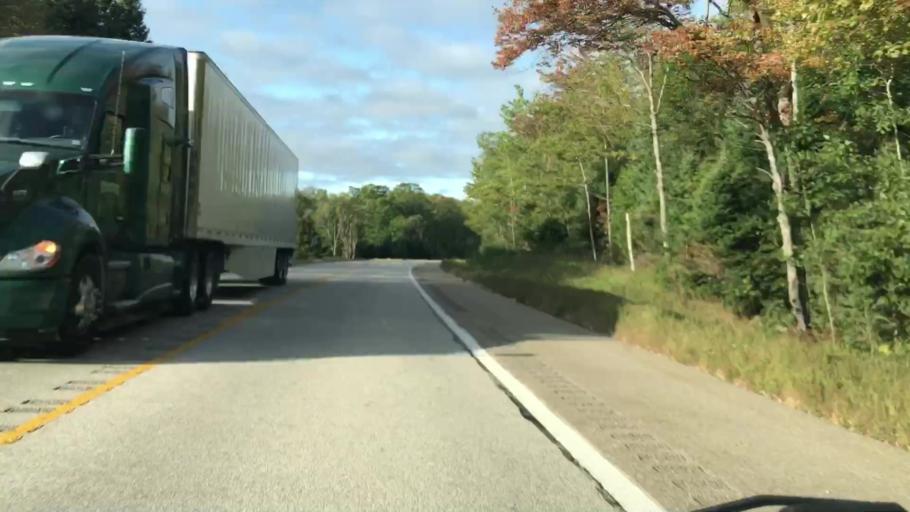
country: US
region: Michigan
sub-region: Luce County
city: Newberry
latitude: 46.3345
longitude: -85.0493
